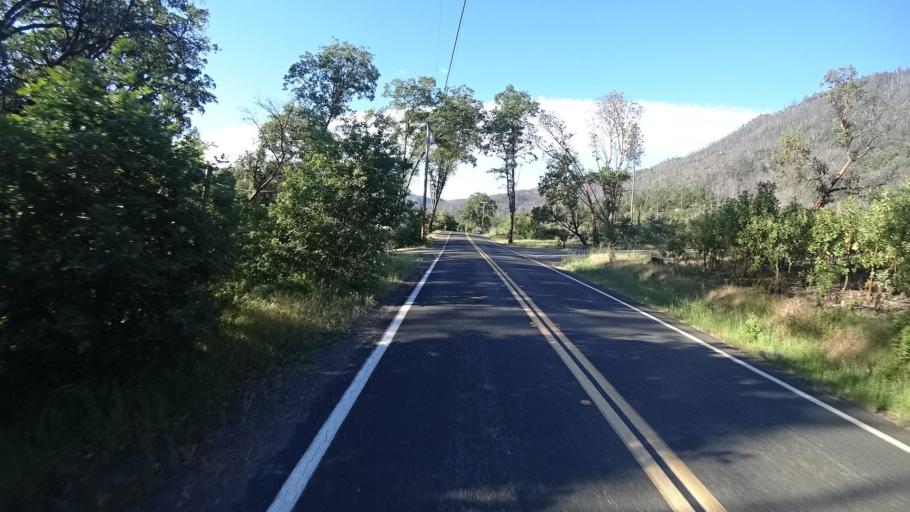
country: US
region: California
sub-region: Lake County
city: Upper Lake
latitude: 39.2366
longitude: -122.9454
